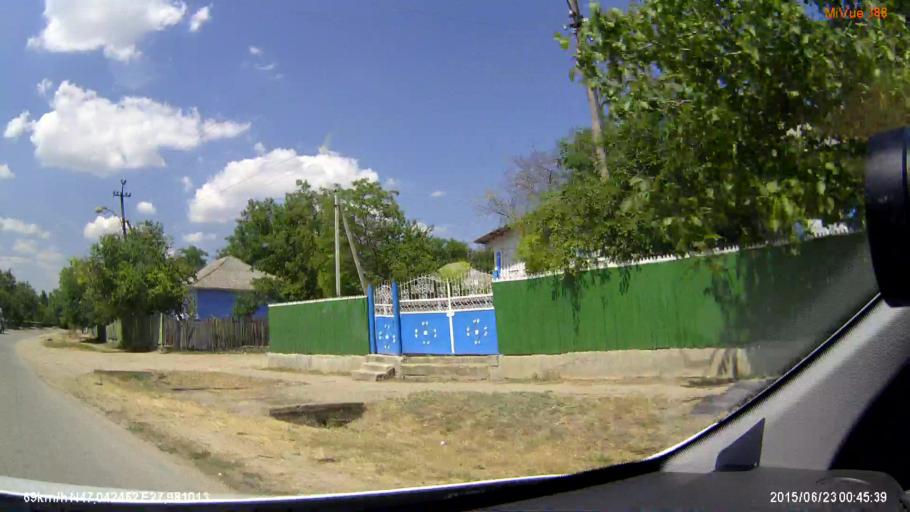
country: RO
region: Iasi
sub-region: Comuna Grozesti
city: Grozesti
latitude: 47.0424
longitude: 27.9812
